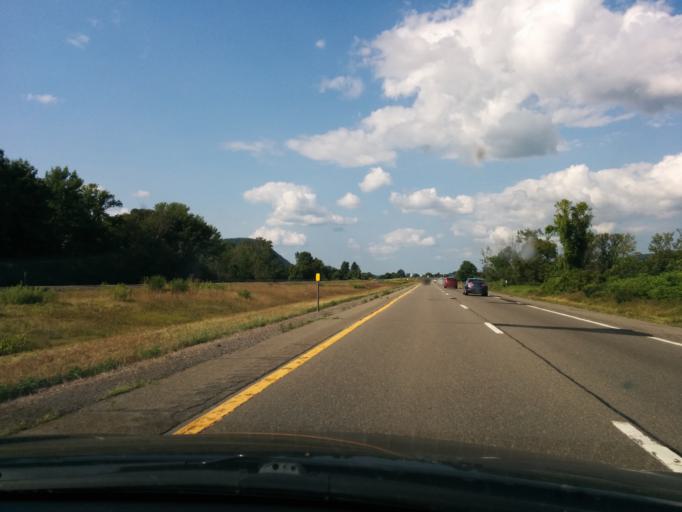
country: US
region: New York
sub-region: Cortland County
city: Homer
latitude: 42.6834
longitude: -76.1626
